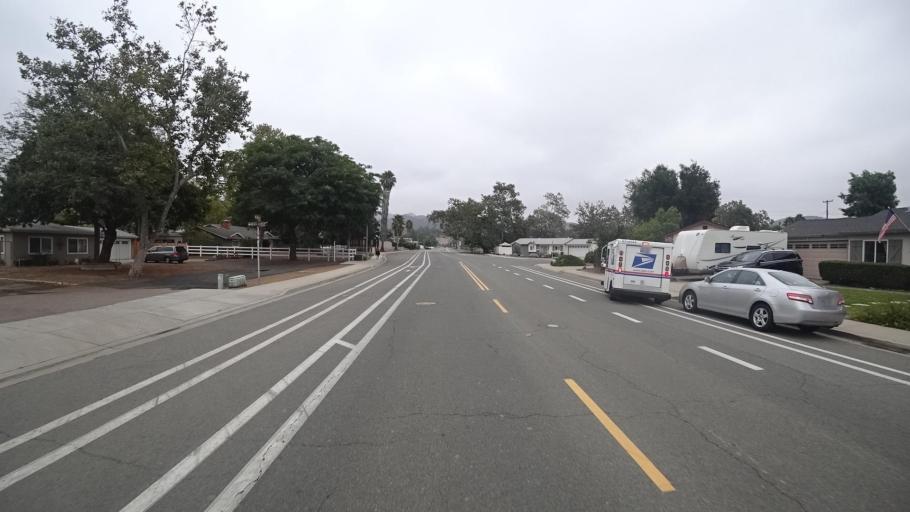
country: US
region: California
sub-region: San Diego County
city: Poway
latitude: 32.9562
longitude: -117.0155
